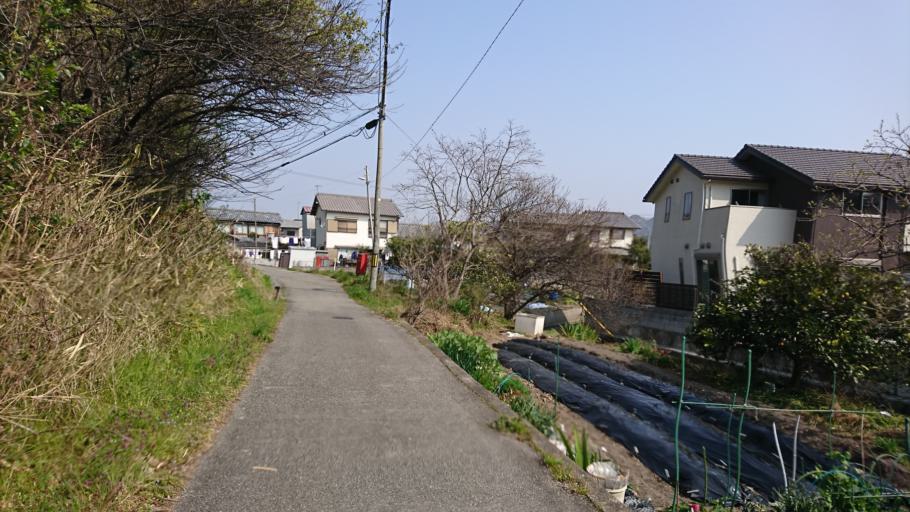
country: JP
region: Hyogo
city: Shirahamacho-usazakiminami
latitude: 34.7893
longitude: 134.7646
